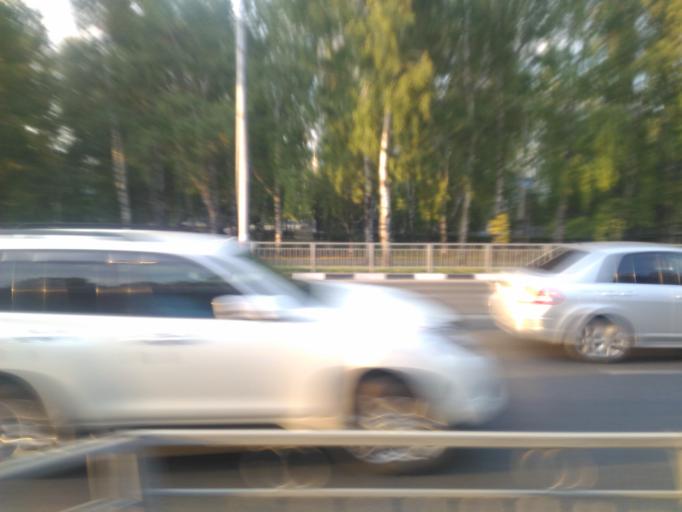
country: RU
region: Ulyanovsk
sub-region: Ulyanovskiy Rayon
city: Ulyanovsk
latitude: 54.3078
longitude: 48.3393
